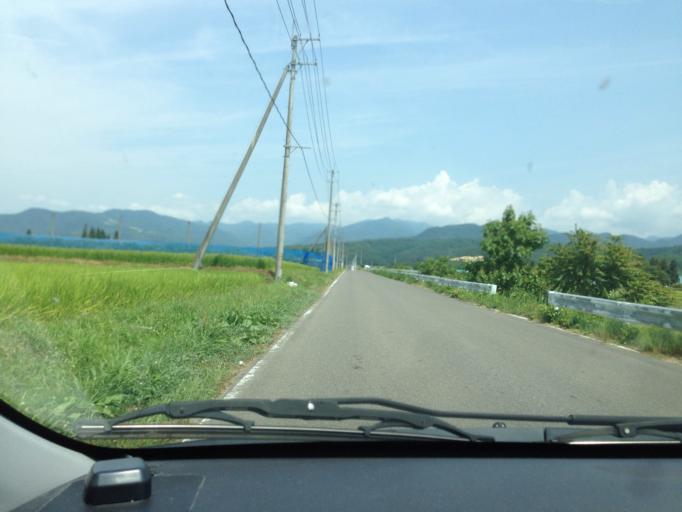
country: JP
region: Fukushima
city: Kitakata
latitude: 37.6802
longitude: 139.8818
